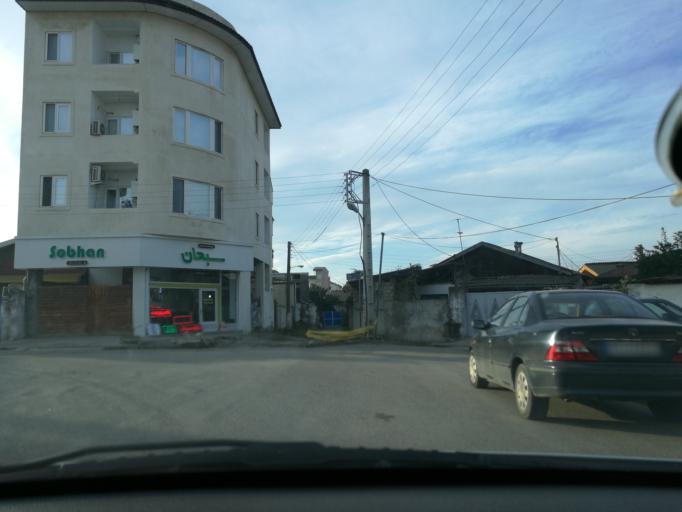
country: IR
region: Mazandaran
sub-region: Nowshahr
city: Nowshahr
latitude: 36.6407
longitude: 51.5033
